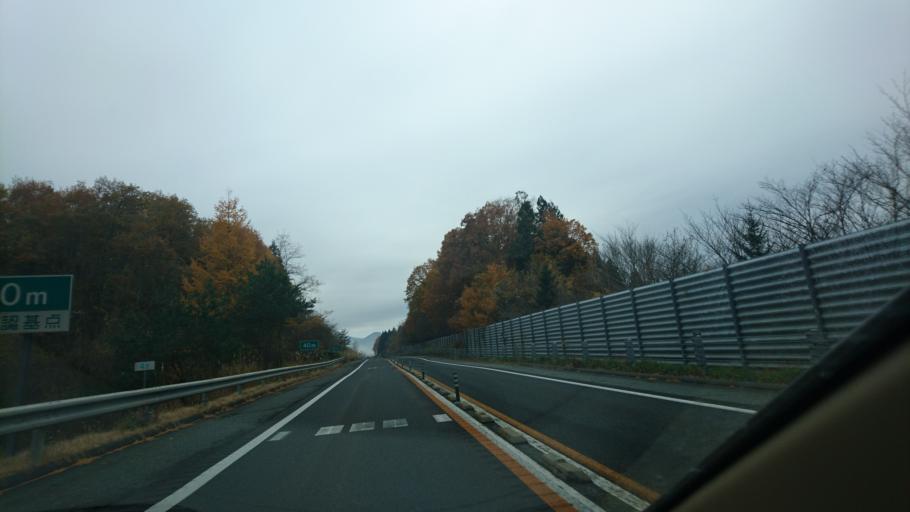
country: JP
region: Iwate
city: Kitakami
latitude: 39.2806
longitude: 141.0321
